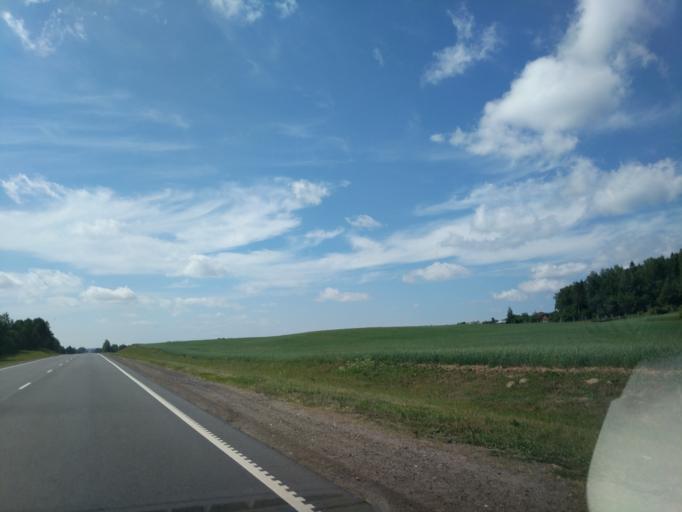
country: BY
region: Minsk
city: Bal'shavik
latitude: 54.0910
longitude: 27.5285
